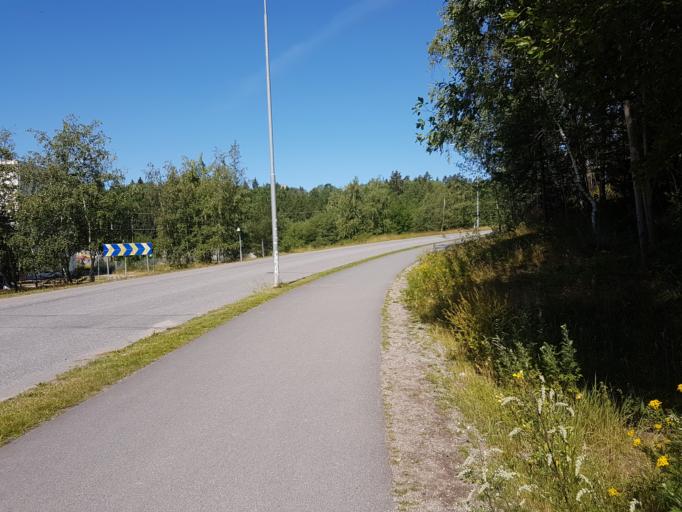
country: SE
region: Stockholm
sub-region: Huddinge Kommun
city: Huddinge
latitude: 59.2145
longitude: 17.9432
